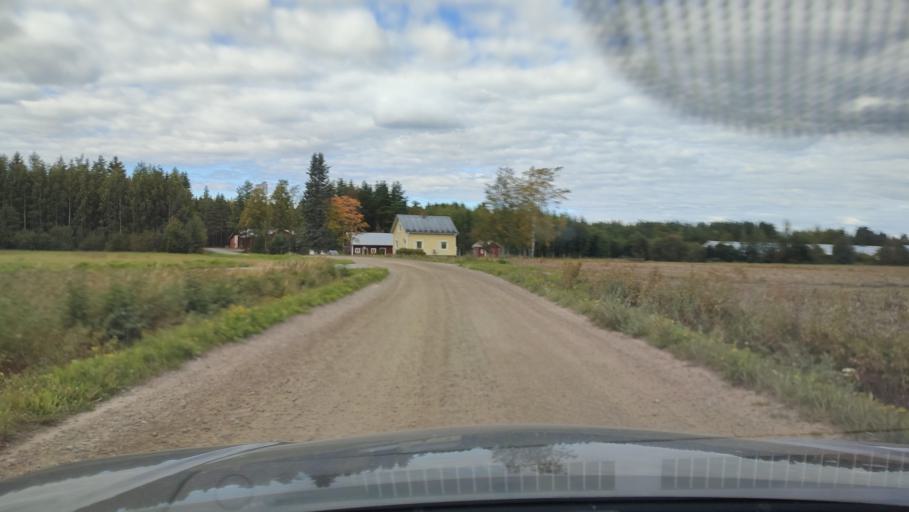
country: FI
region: Southern Ostrobothnia
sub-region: Suupohja
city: Karijoki
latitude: 62.2356
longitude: 21.6028
